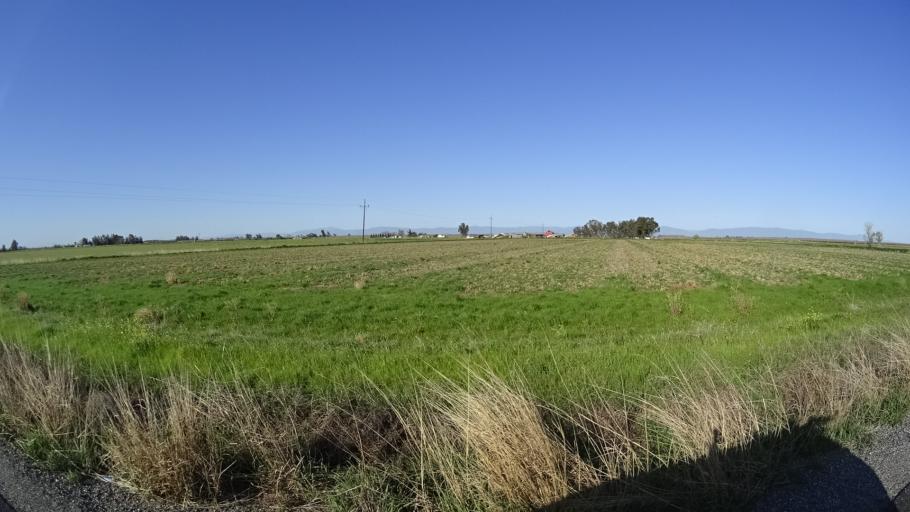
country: US
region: California
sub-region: Glenn County
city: Orland
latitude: 39.7776
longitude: -122.1147
